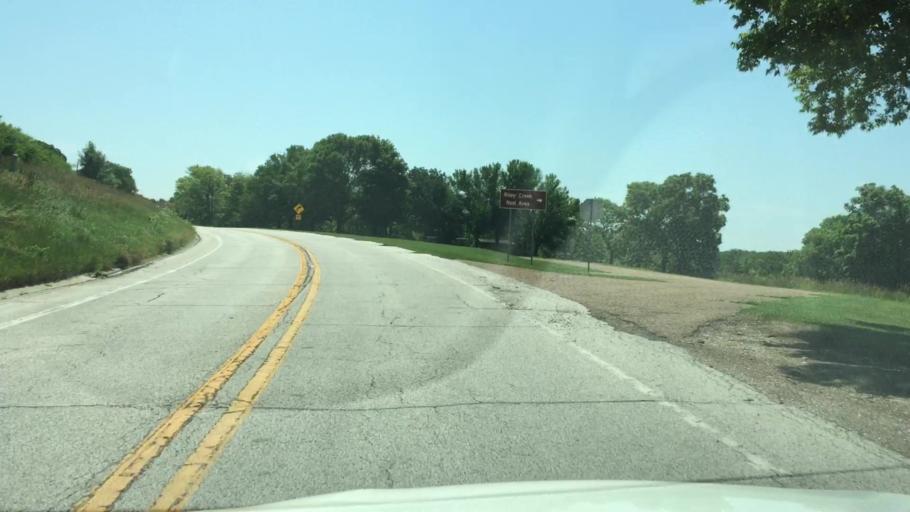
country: US
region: Illinois
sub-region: Hancock County
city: Nauvoo
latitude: 40.5200
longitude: -91.3637
